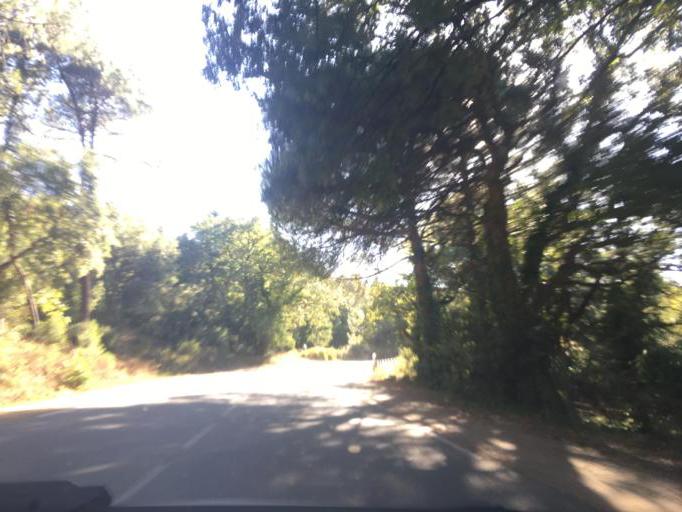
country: FR
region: Provence-Alpes-Cote d'Azur
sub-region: Departement du Var
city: La Garde-Freinet
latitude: 43.3024
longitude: 6.4830
